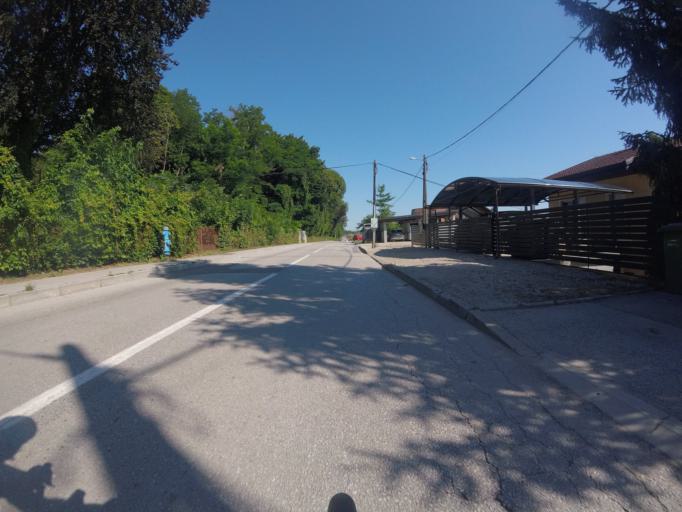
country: HR
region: Zagrebacka
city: Bregana
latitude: 45.8217
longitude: 15.6989
